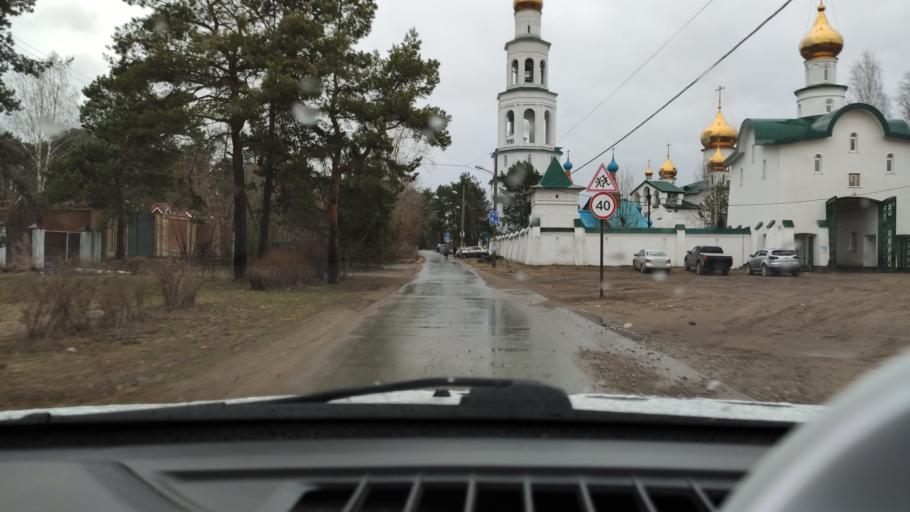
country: RU
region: Perm
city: Perm
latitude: 58.0475
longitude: 56.2904
